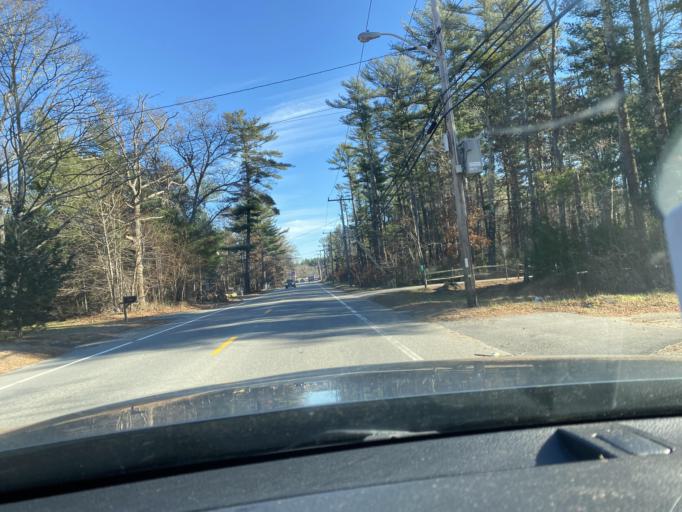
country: US
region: Massachusetts
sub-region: Plymouth County
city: West Wareham
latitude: 41.8004
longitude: -70.7704
